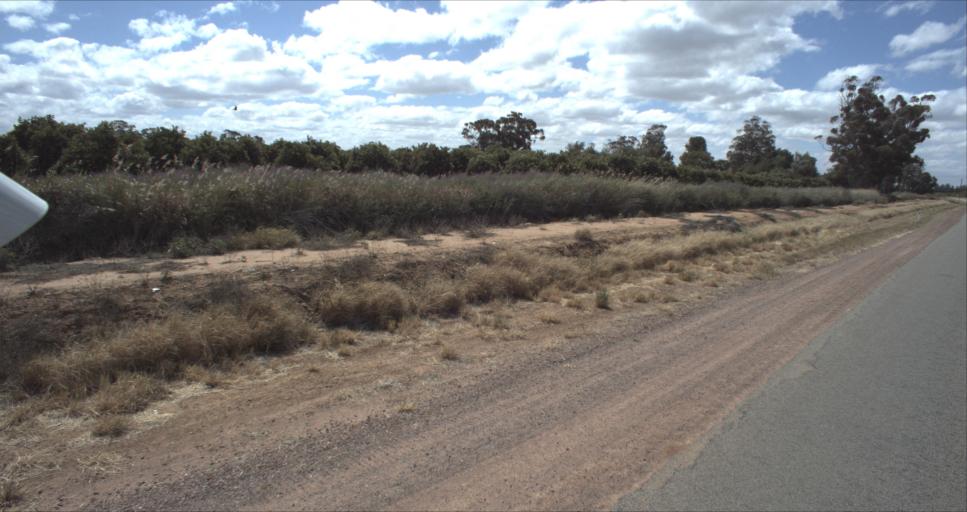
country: AU
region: New South Wales
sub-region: Leeton
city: Leeton
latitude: -34.5891
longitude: 146.3703
